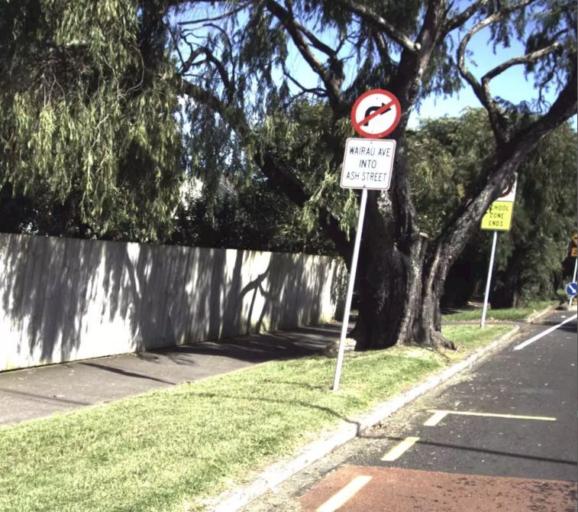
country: NZ
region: Auckland
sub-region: Auckland
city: Rosebank
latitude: -36.8911
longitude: 174.6881
